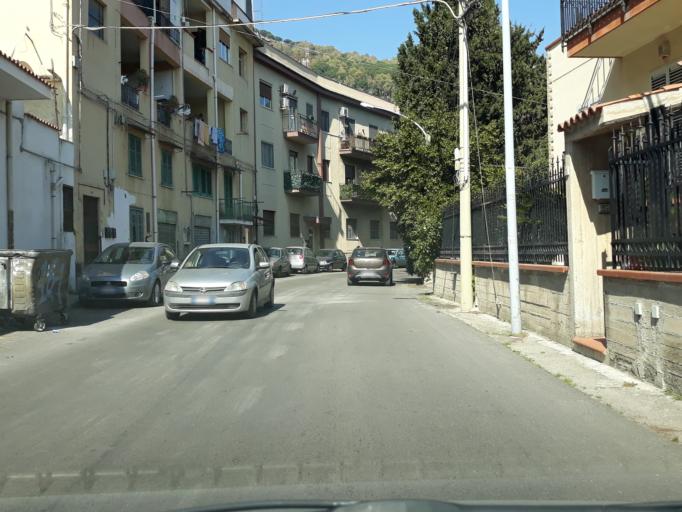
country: IT
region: Sicily
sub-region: Palermo
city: Piano dei Geli
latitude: 38.1167
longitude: 13.2886
